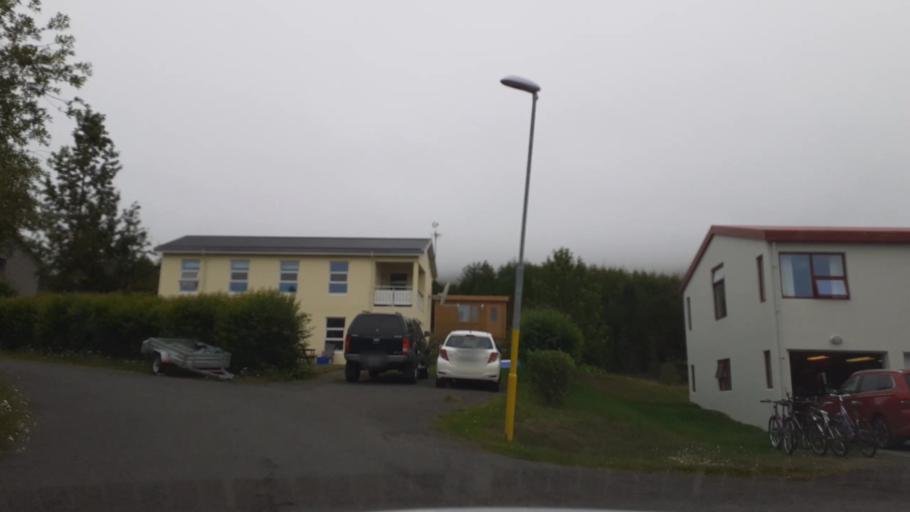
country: IS
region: Northeast
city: Siglufjoerdur
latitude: 65.7317
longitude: -19.1093
